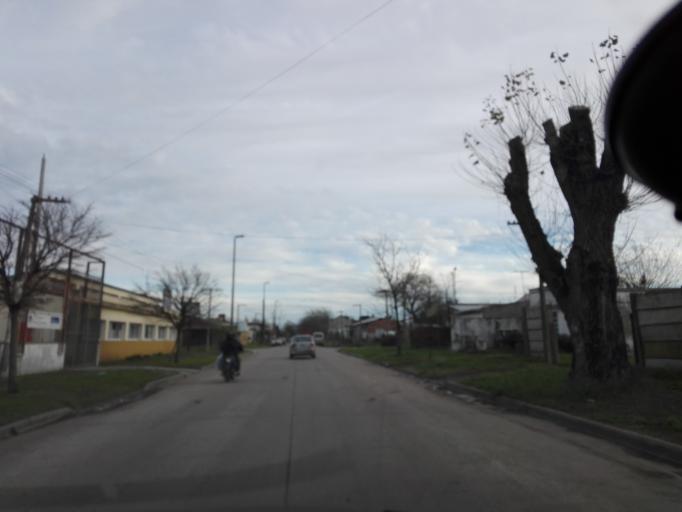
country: AR
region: Buenos Aires
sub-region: Partido de Balcarce
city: Balcarce
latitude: -37.8423
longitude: -58.2464
